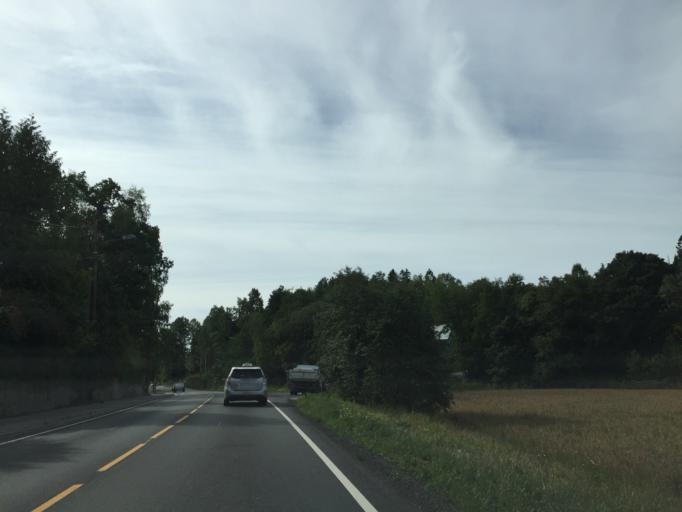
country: NO
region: Ostfold
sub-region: Moss
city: Moss
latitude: 59.4700
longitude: 10.6900
